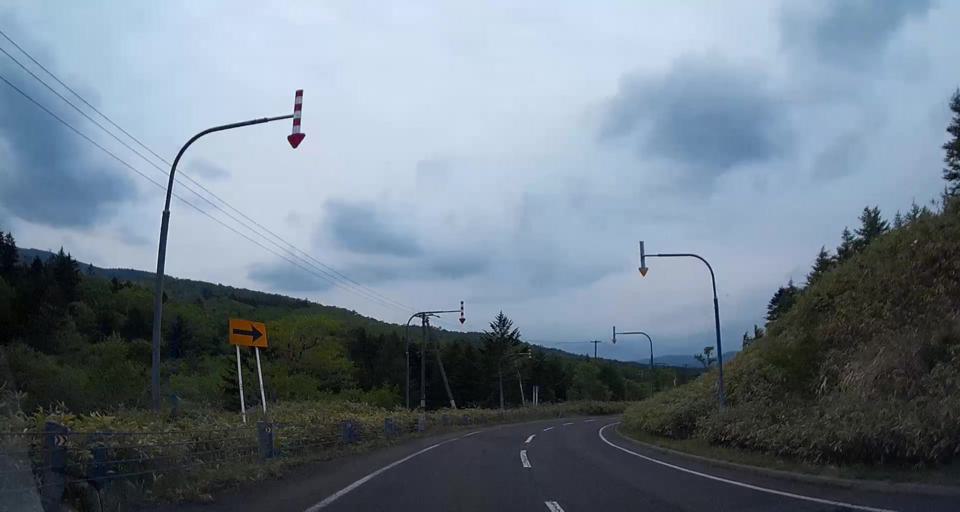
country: JP
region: Hokkaido
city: Shiraoi
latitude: 42.6722
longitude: 141.1630
